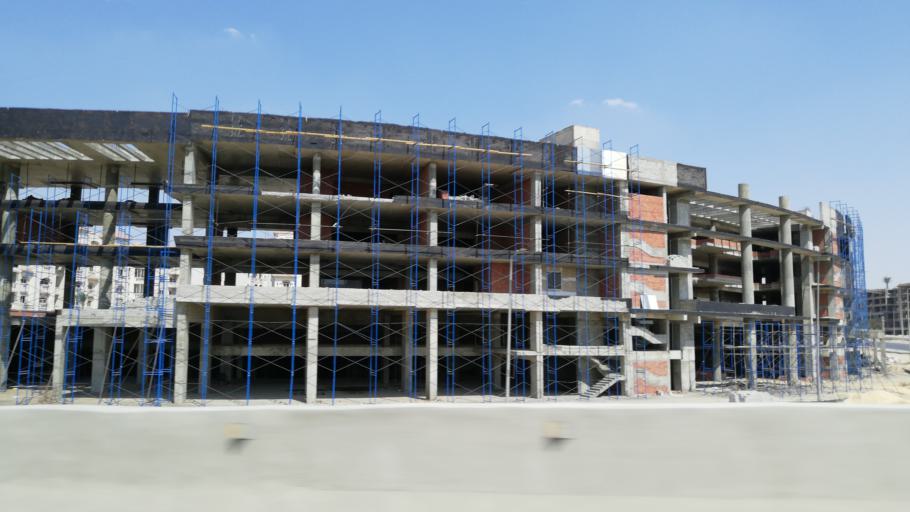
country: EG
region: Muhafazat al Qalyubiyah
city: Al Khankah
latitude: 30.0297
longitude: 31.4750
